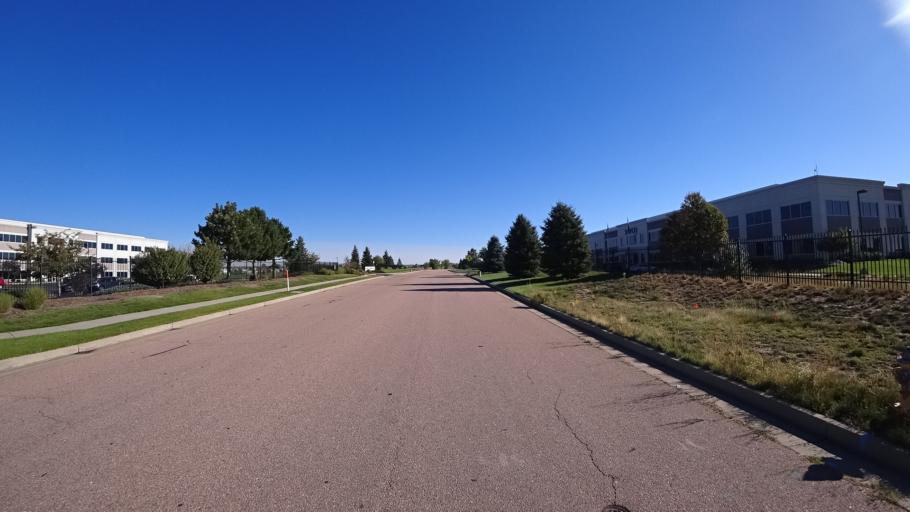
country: US
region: Colorado
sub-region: El Paso County
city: Cimarron Hills
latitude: 38.8163
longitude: -104.7272
